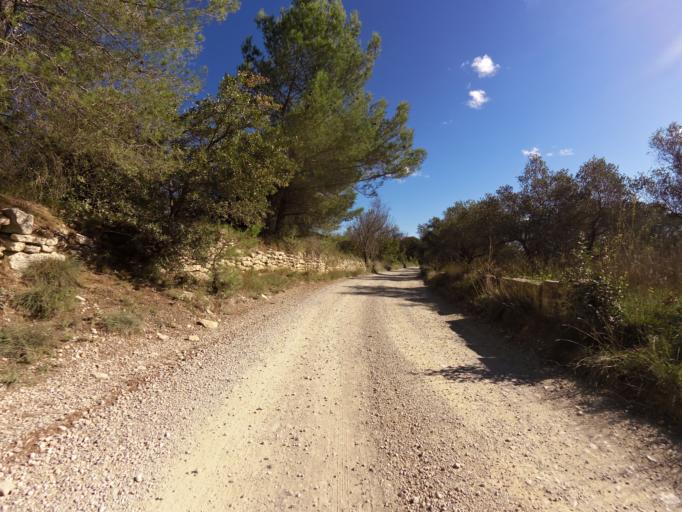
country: FR
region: Languedoc-Roussillon
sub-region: Departement du Gard
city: Aubais
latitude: 43.7427
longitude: 4.1517
